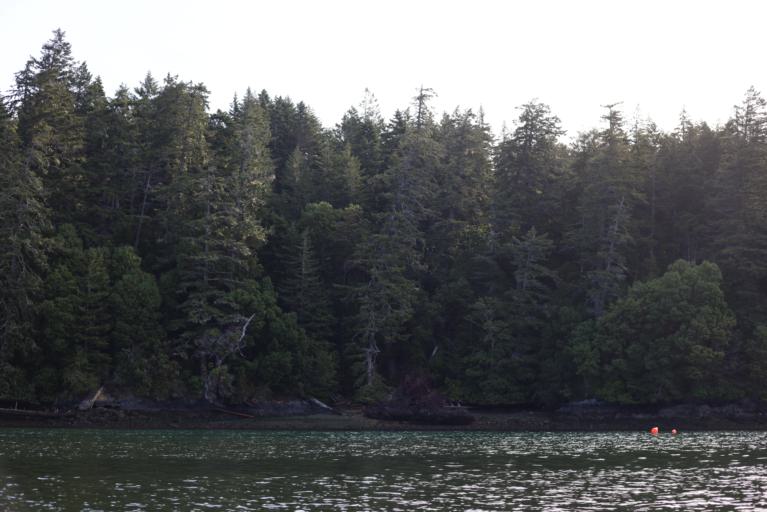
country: CA
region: British Columbia
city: Metchosin
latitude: 48.3423
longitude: -123.5572
